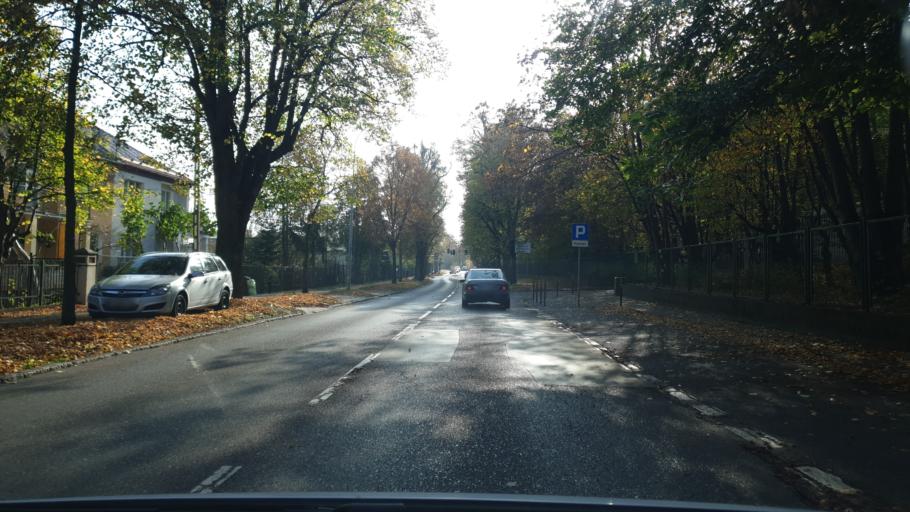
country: PL
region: Pomeranian Voivodeship
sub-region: Sopot
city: Sopot
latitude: 54.3999
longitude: 18.5627
